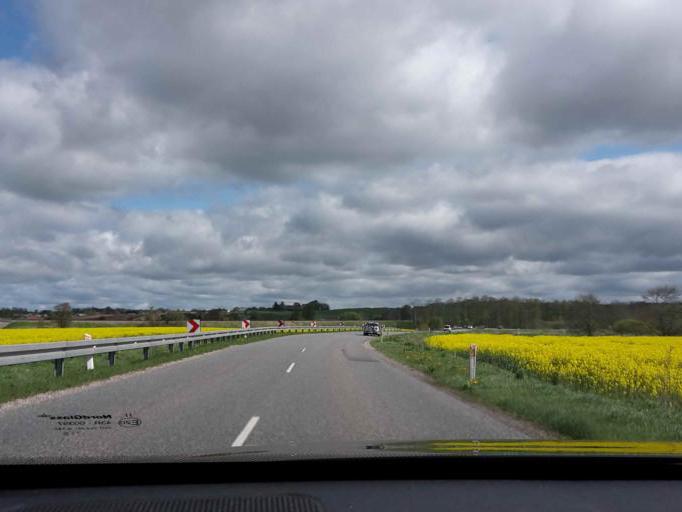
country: DK
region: Central Jutland
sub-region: Syddjurs Kommune
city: Hornslet
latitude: 56.3412
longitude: 10.3382
